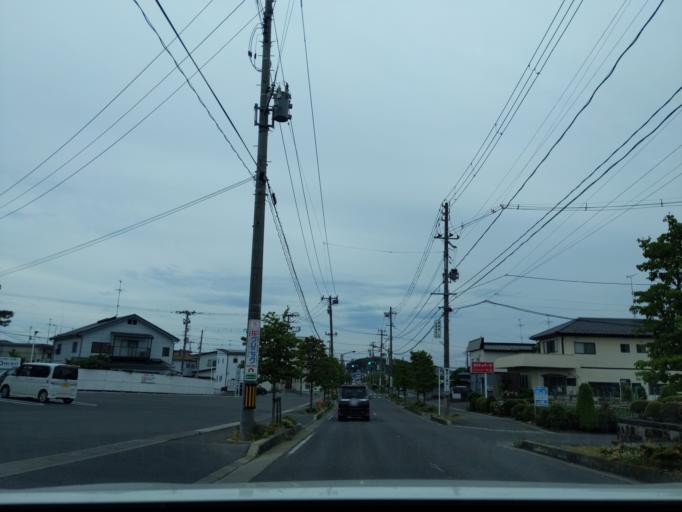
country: JP
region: Fukushima
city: Koriyama
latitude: 37.3727
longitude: 140.3647
